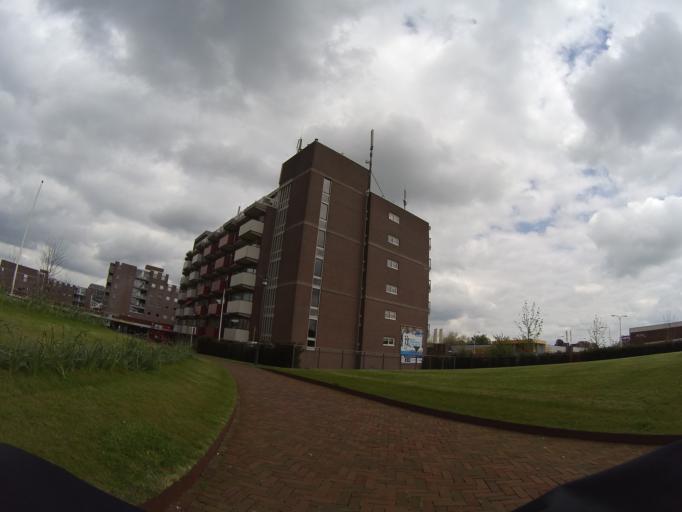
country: NL
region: Overijssel
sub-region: Gemeente Hardenberg
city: Hardenberg
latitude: 52.5737
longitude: 6.6195
